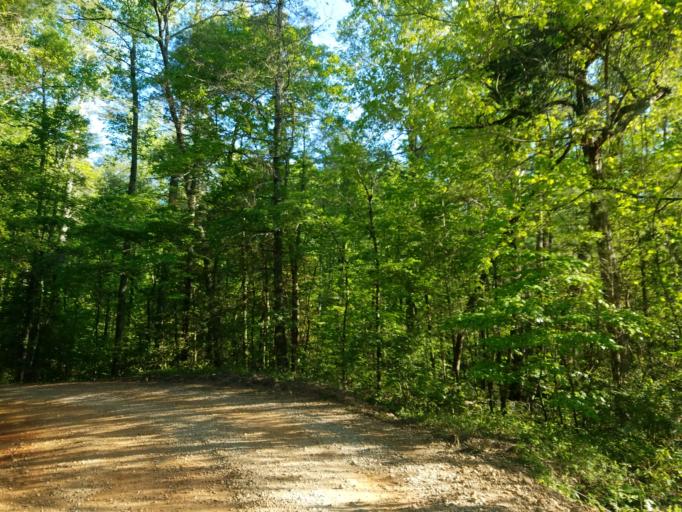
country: US
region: Georgia
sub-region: Fannin County
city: Blue Ridge
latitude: 34.7315
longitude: -84.1548
